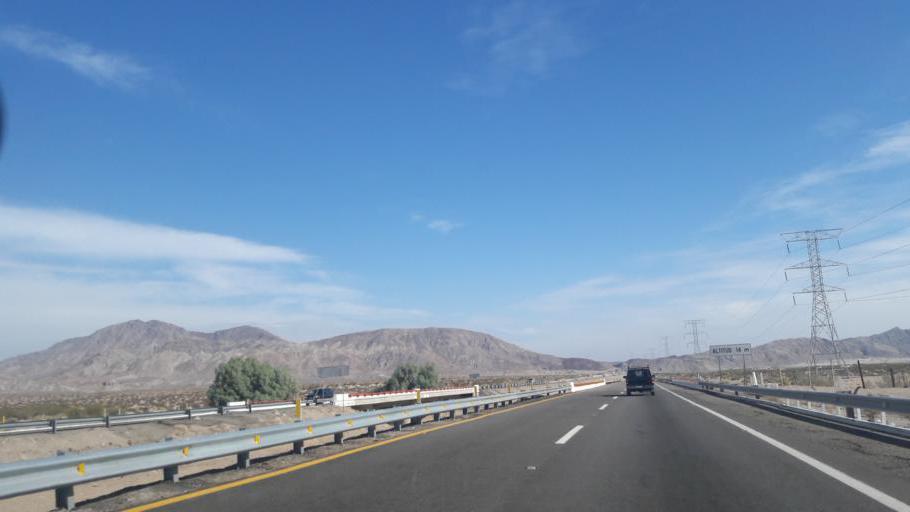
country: MX
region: Baja California
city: Progreso
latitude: 32.5738
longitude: -115.7708
